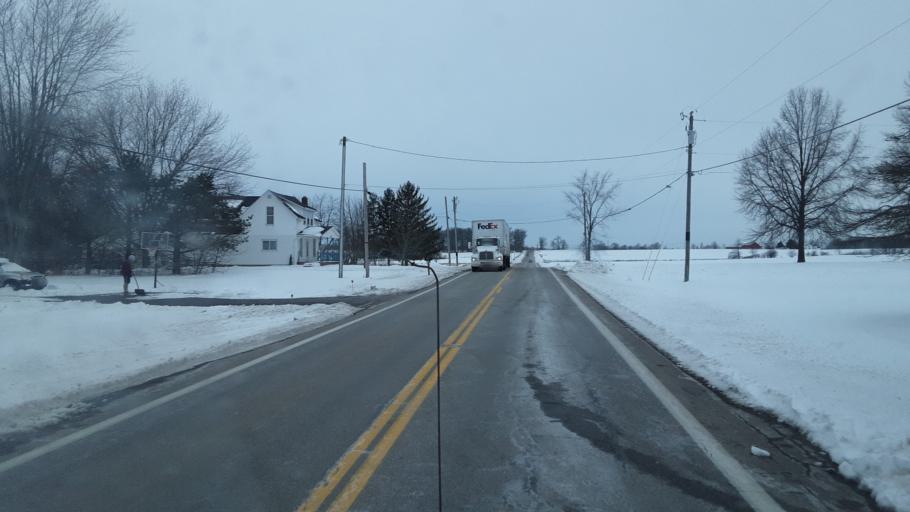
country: US
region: Ohio
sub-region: Union County
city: Marysville
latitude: 40.1783
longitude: -83.3326
